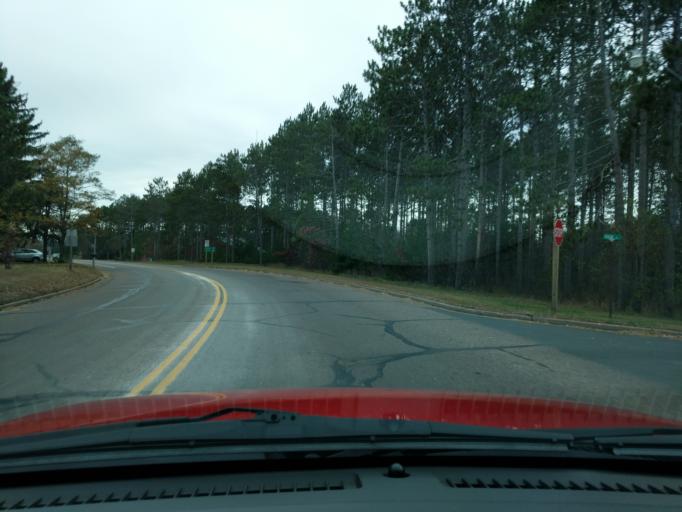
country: US
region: Wisconsin
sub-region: Washburn County
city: Spooner
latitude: 45.8237
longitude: -91.8935
